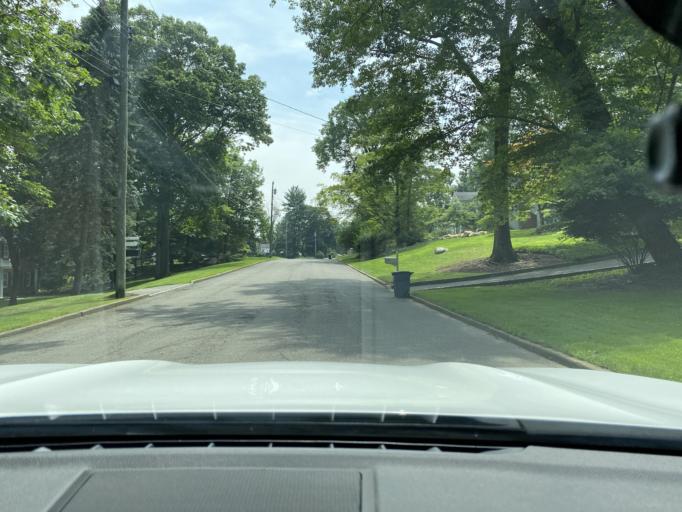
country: US
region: New Jersey
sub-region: Bergen County
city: Upper Saddle River
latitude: 41.0802
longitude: -74.1044
